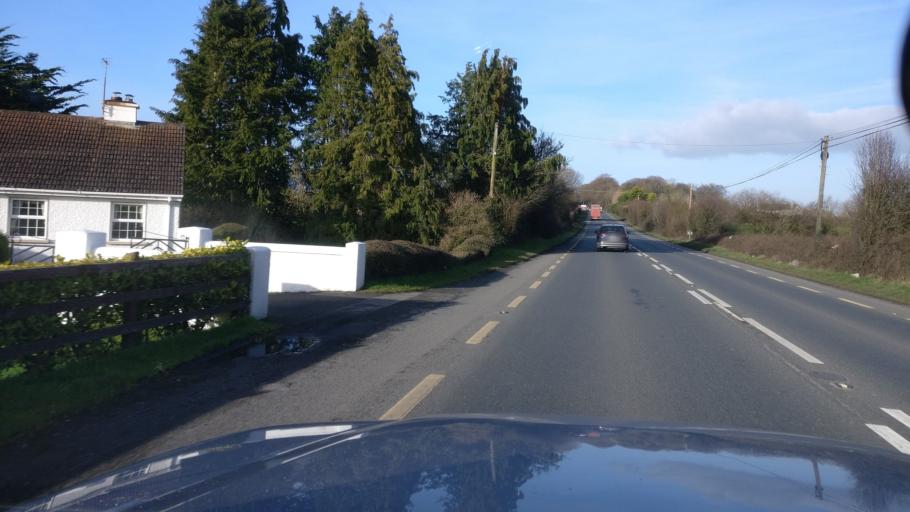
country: IE
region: Leinster
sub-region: Uibh Fhaili
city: Tullamore
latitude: 53.2476
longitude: -7.4774
